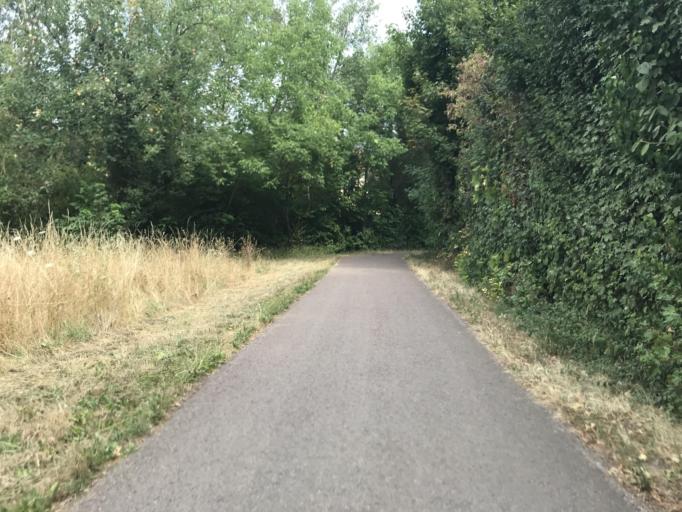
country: DE
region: Rheinland-Pfalz
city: Hahnheim
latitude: 49.8594
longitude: 8.2459
